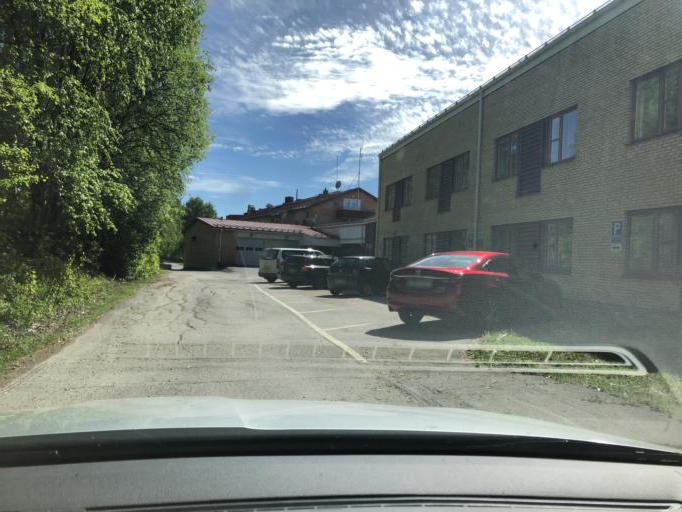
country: SE
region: Norrbotten
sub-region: Alvsbyns Kommun
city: AElvsbyn
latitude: 65.6699
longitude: 21.0129
